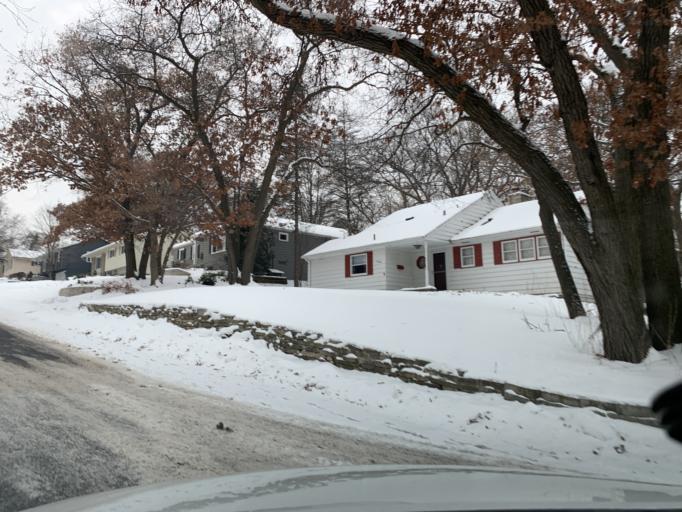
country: US
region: Minnesota
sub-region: Hennepin County
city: Edina
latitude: 44.9169
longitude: -93.3568
